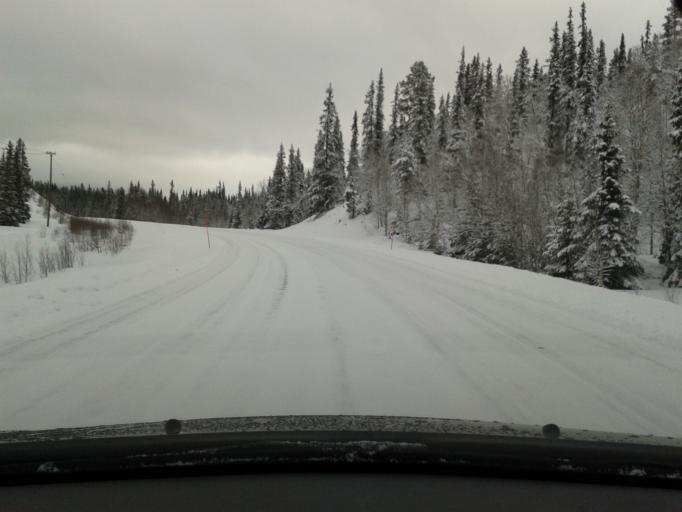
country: SE
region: Vaesterbotten
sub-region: Vilhelmina Kommun
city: Sjoberg
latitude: 65.2411
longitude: 15.7736
